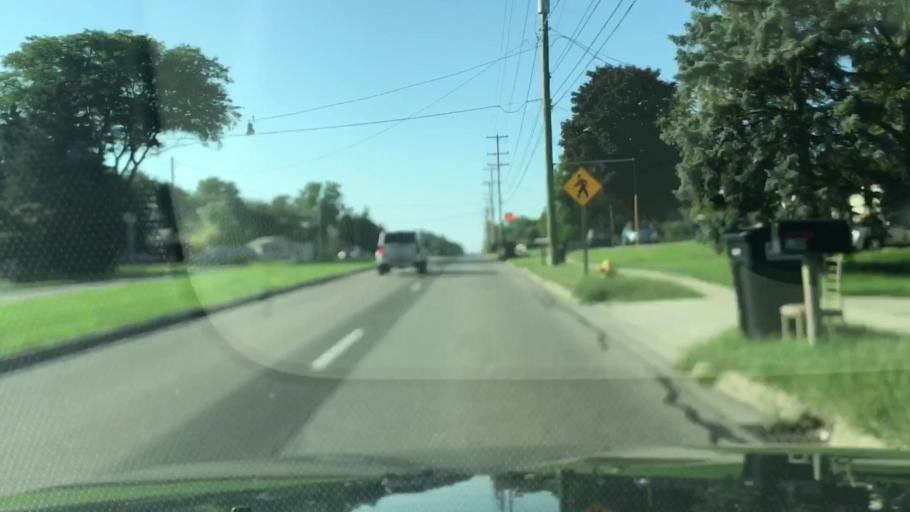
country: US
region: Michigan
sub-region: Kent County
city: Kentwood
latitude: 42.8661
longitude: -85.6253
